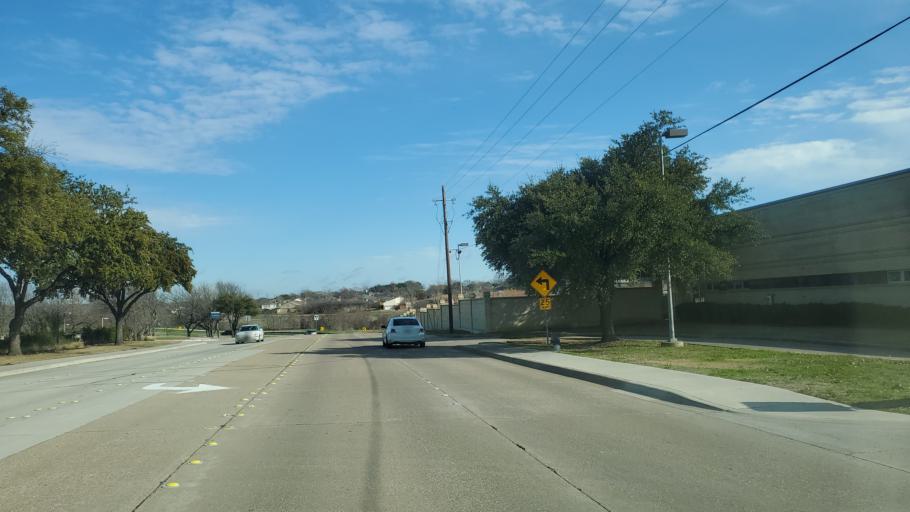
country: US
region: Texas
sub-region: Dallas County
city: Carrollton
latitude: 32.9755
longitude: -96.8867
